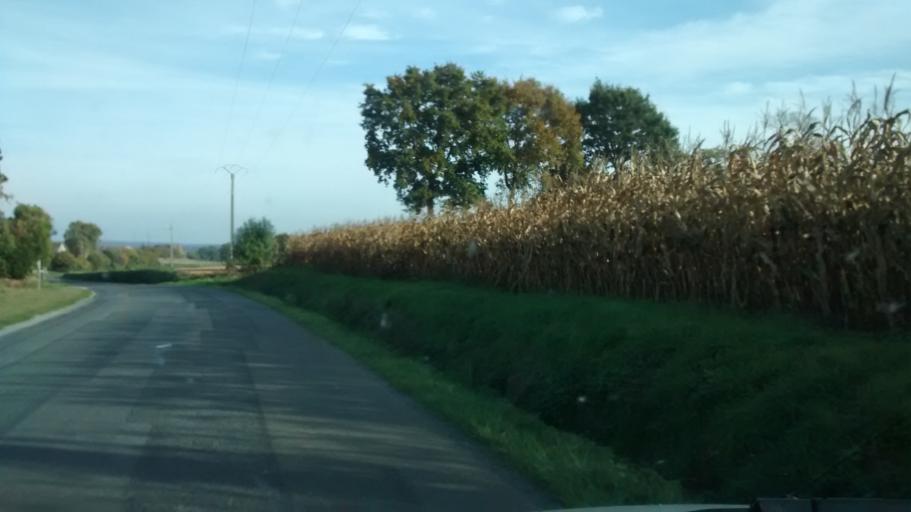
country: FR
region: Brittany
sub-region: Departement d'Ille-et-Vilaine
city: Betton
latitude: 48.1895
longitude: -1.6644
